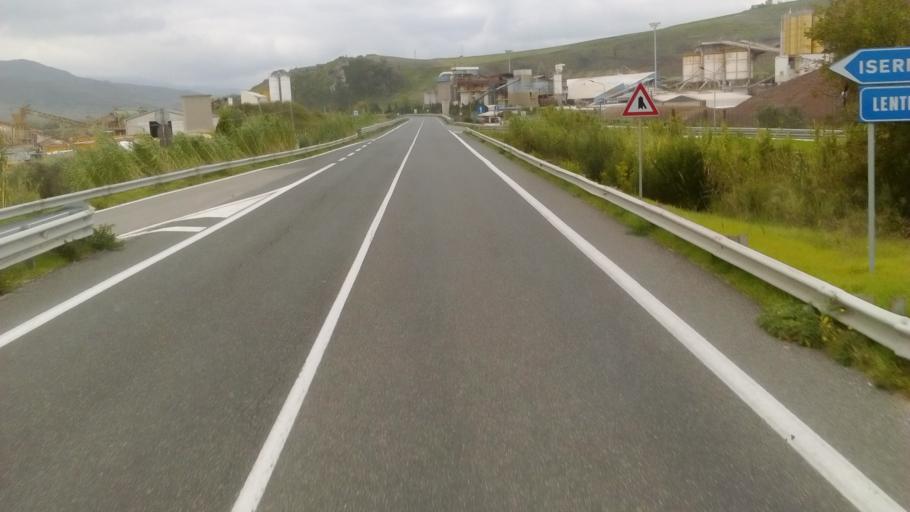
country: IT
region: Abruzzo
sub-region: Provincia di Chieti
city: Lentella
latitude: 41.9970
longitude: 14.7156
